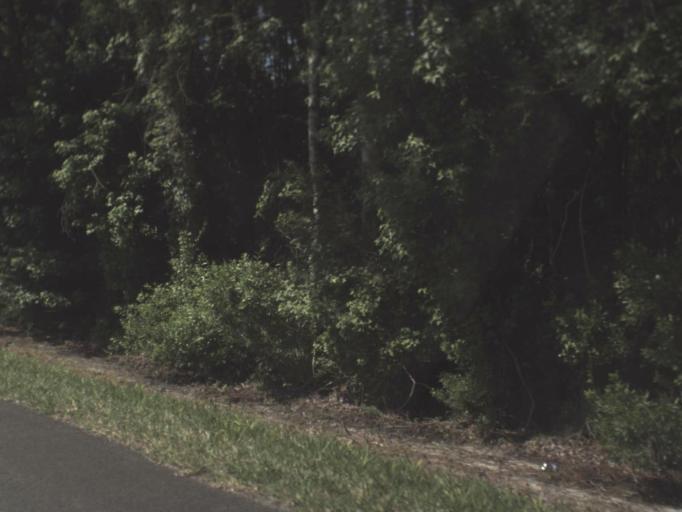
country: US
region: Florida
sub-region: Nassau County
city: Nassau Village-Ratliff
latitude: 30.4719
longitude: -81.7101
